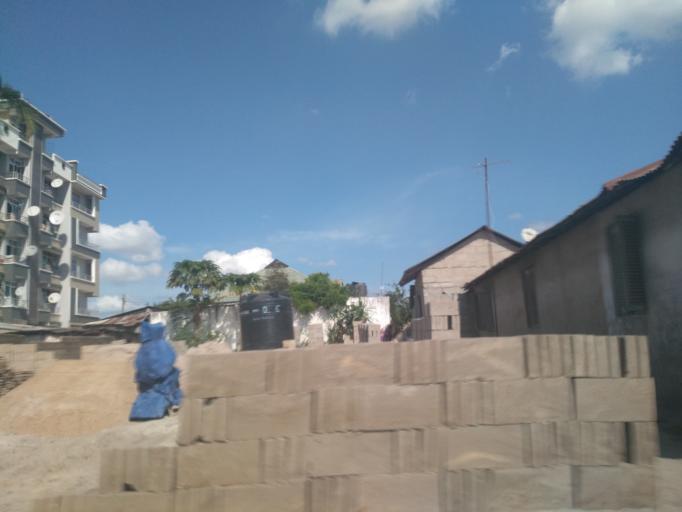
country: TZ
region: Dar es Salaam
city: Dar es Salaam
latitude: -6.8646
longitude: 39.2566
